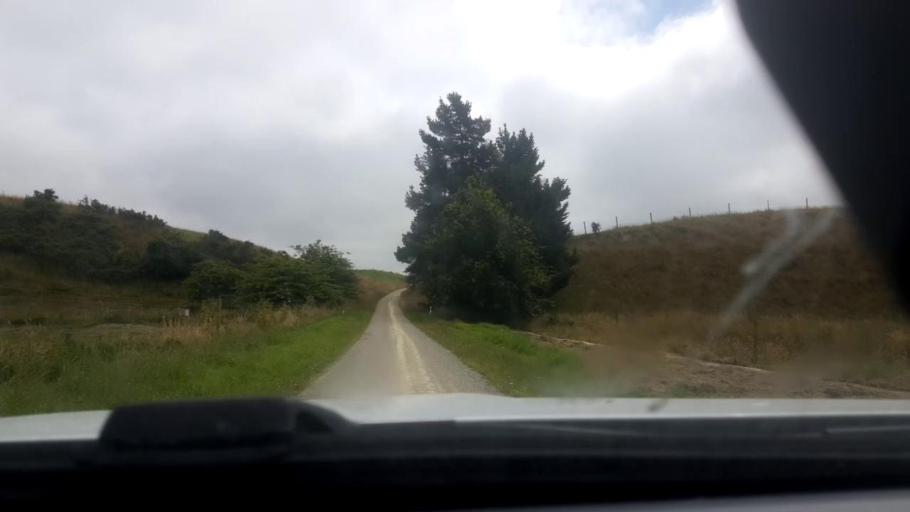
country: NZ
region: Canterbury
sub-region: Timaru District
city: Pleasant Point
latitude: -44.2154
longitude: 171.1077
